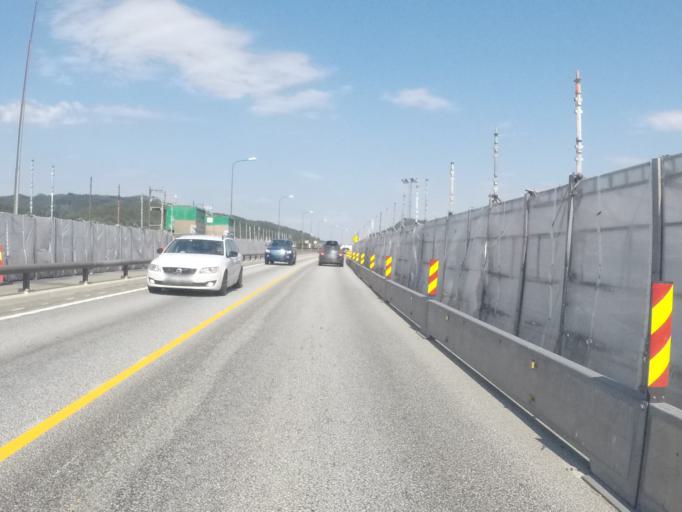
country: NO
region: Hordaland
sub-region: Meland
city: Frekhaug
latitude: 60.5240
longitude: 5.2643
